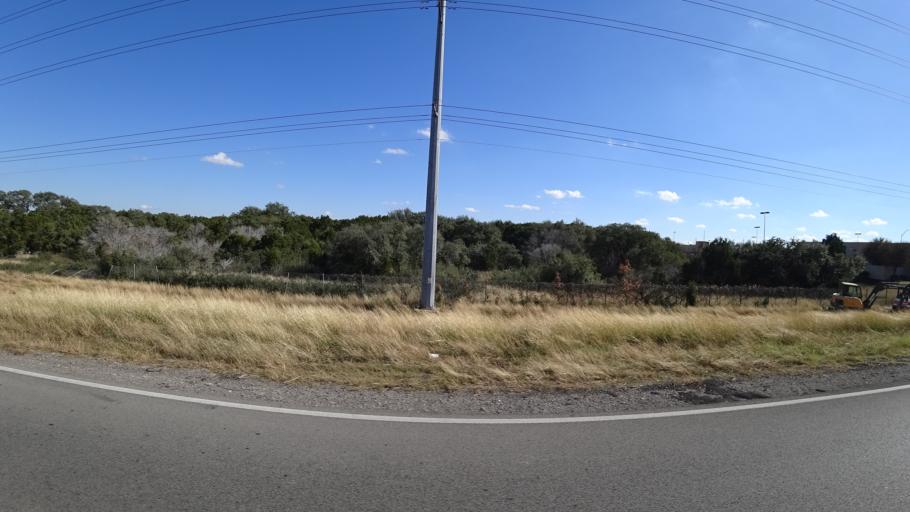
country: US
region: Texas
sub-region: Travis County
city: Shady Hollow
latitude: 30.2017
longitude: -97.8648
